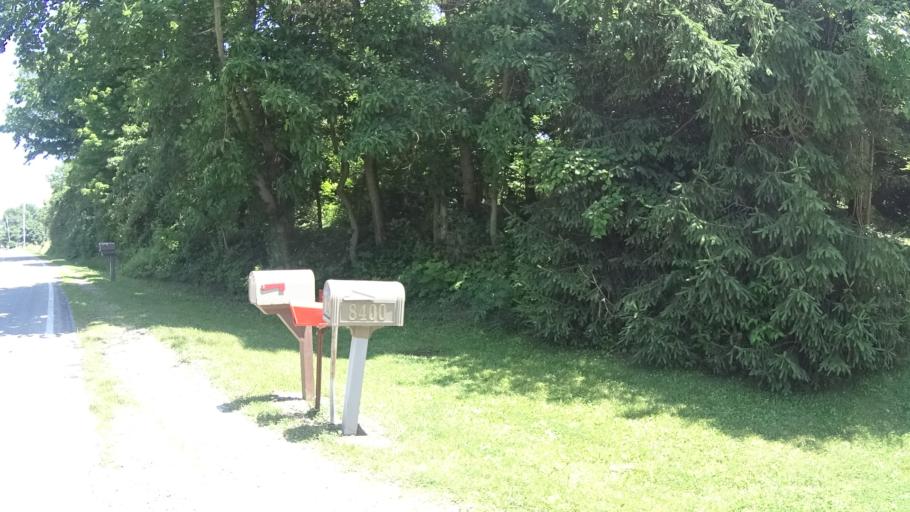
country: US
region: Ohio
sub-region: Lorain County
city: Vermilion
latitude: 41.3548
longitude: -82.3994
